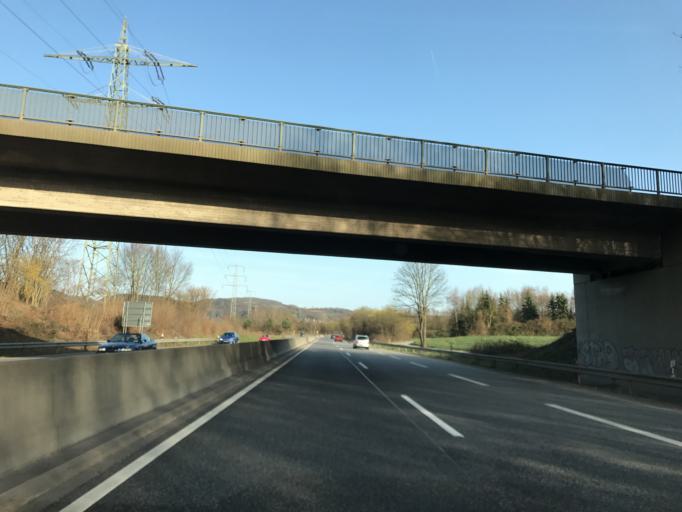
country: DE
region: Rheinland-Pfalz
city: Kaltenengers
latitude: 50.4327
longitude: 7.5452
